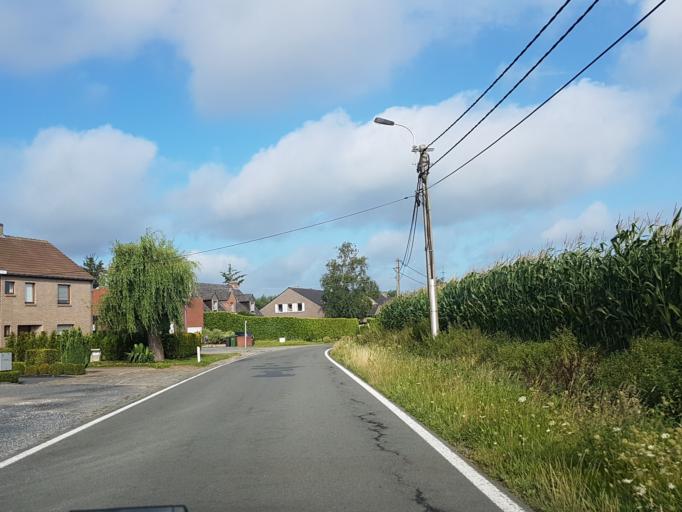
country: BE
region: Flanders
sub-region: Provincie Oost-Vlaanderen
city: Sint-Martens-Latem
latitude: 51.0592
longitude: 3.6392
